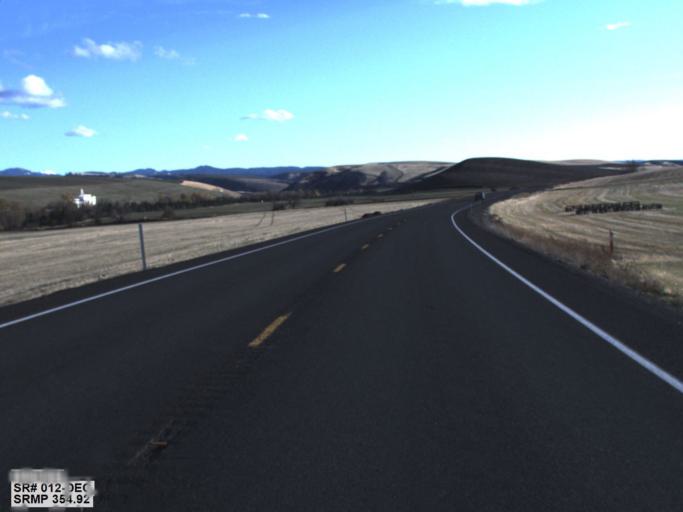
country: US
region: Washington
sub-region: Walla Walla County
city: Waitsburg
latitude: 46.2336
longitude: -118.1386
